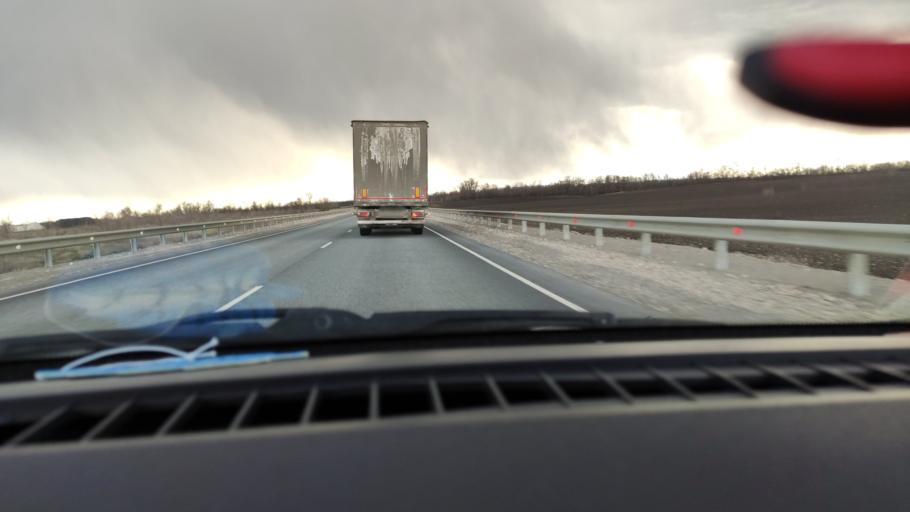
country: RU
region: Saratov
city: Yelshanka
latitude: 51.8472
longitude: 46.4849
